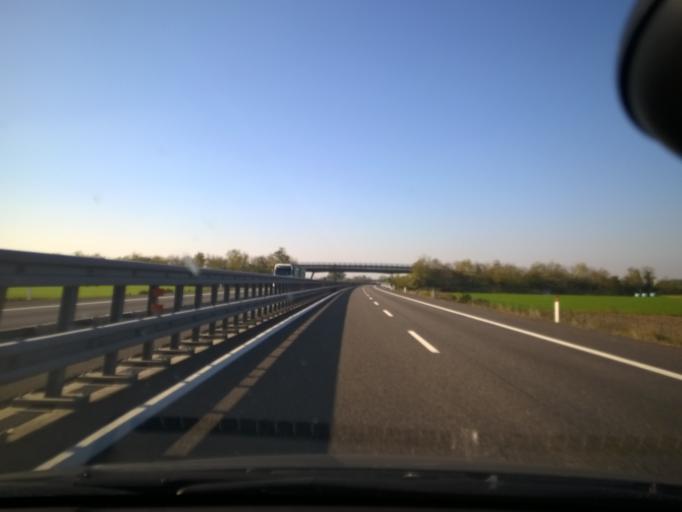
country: IT
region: Emilia-Romagna
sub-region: Provincia di Piacenza
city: Rottofreno
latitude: 45.0659
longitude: 9.5322
